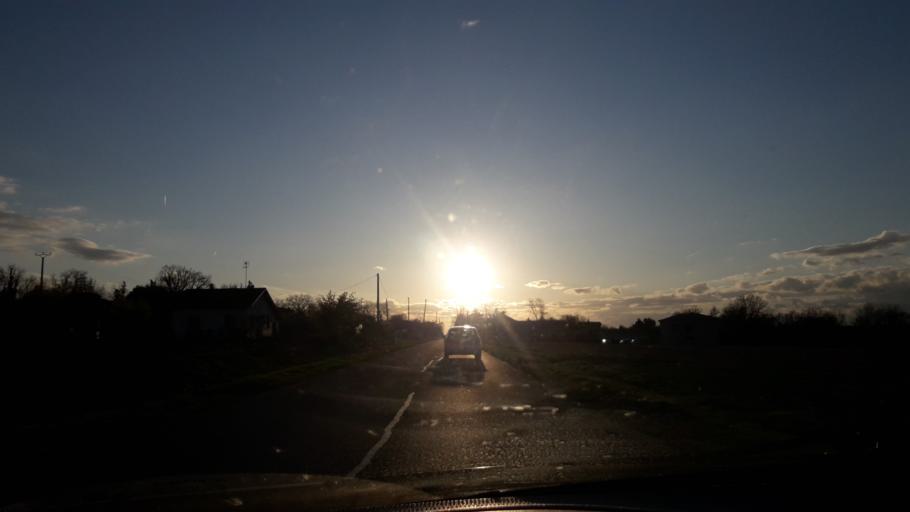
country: FR
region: Midi-Pyrenees
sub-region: Departement du Gers
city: Pujaudran
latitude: 43.6235
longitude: 1.1110
